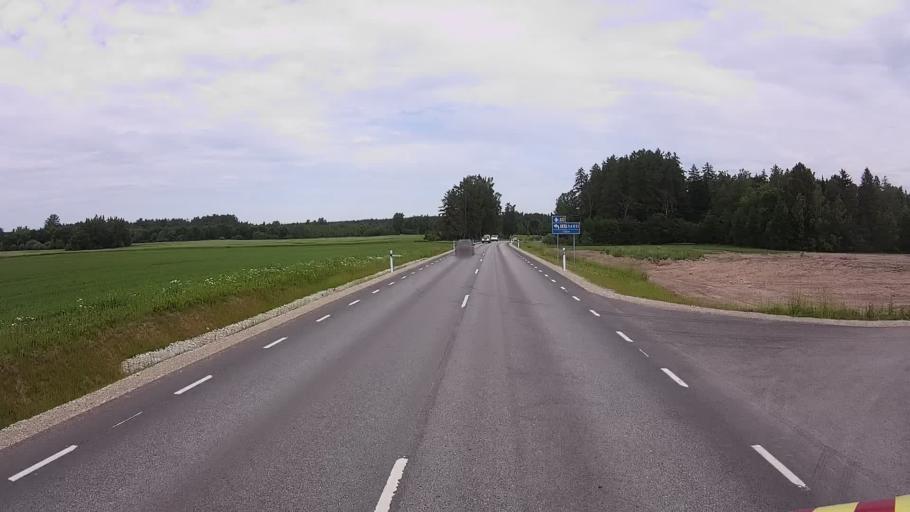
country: EE
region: Viljandimaa
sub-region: Viljandi linn
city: Viljandi
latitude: 58.2766
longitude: 25.5827
